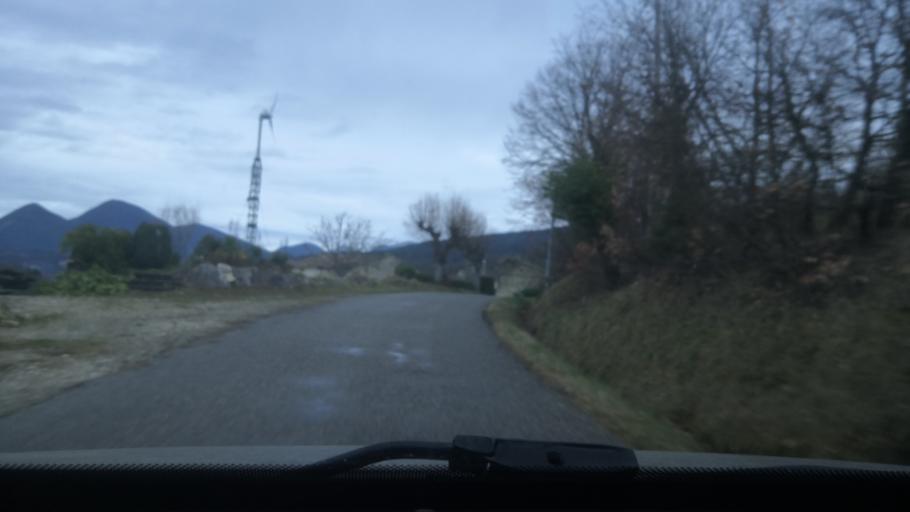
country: FR
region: Rhone-Alpes
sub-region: Departement de la Drome
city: Dieulefit
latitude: 44.5172
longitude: 5.0348
